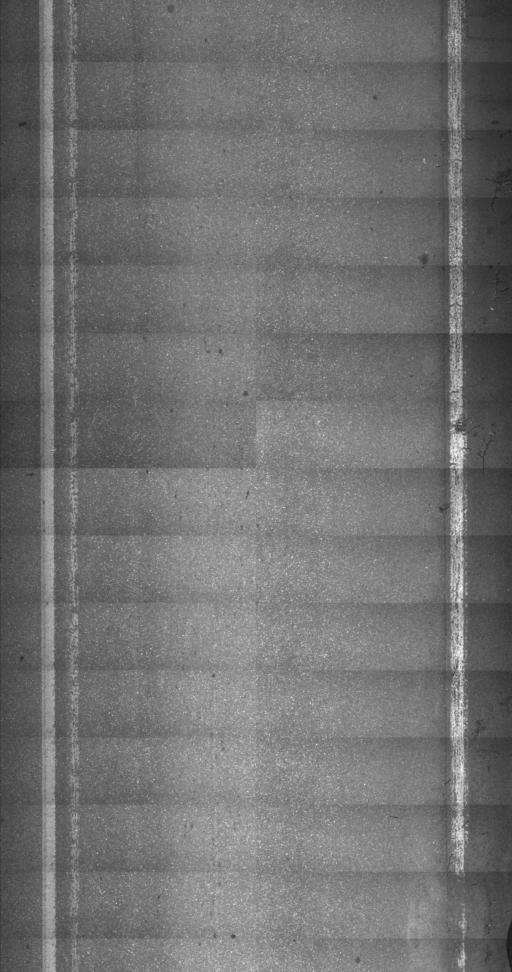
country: US
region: Vermont
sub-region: Chittenden County
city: Burlington
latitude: 44.4824
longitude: -73.2058
